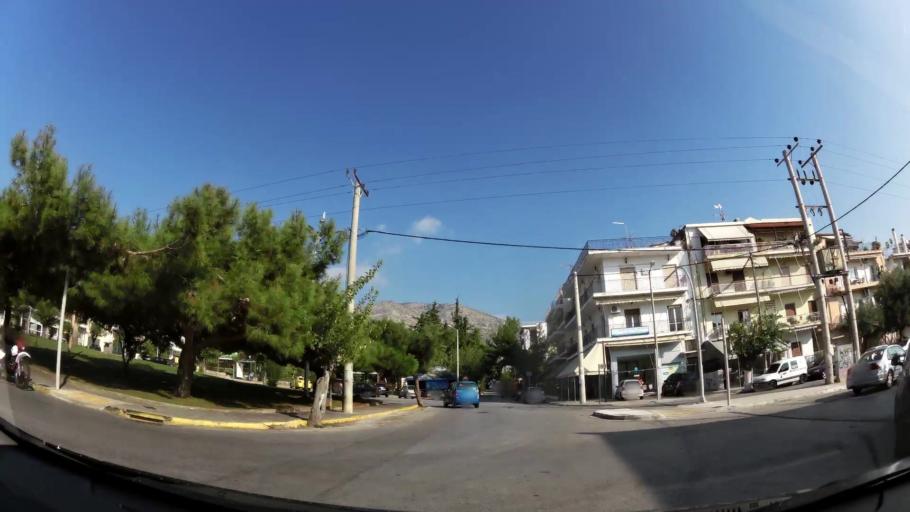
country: GR
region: Attica
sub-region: Nomarchia Athinas
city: Argyroupoli
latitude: 37.9146
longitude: 23.7499
